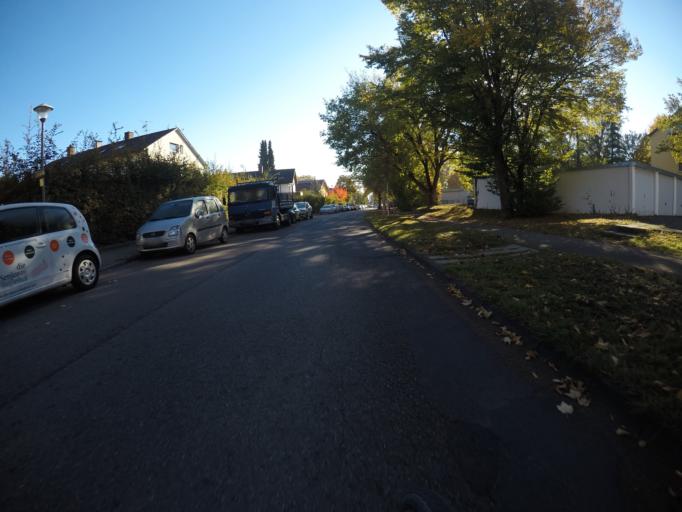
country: DE
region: Baden-Wuerttemberg
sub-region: Regierungsbezirk Stuttgart
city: Steinenbronn
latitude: 48.7180
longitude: 9.1204
